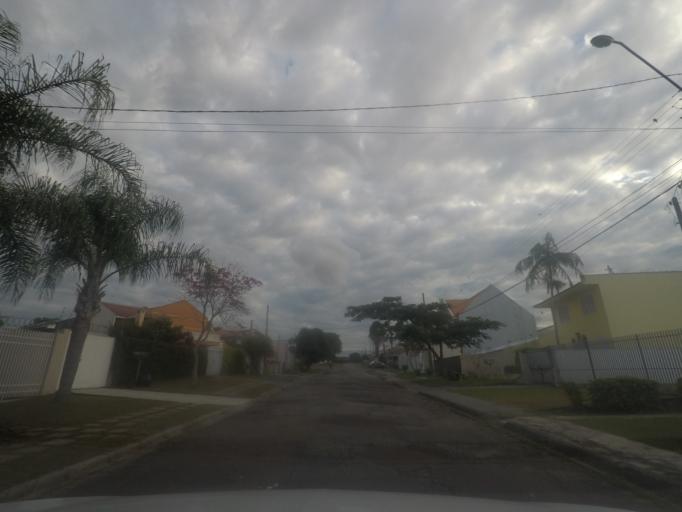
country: BR
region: Parana
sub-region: Pinhais
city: Pinhais
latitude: -25.4673
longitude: -49.2115
